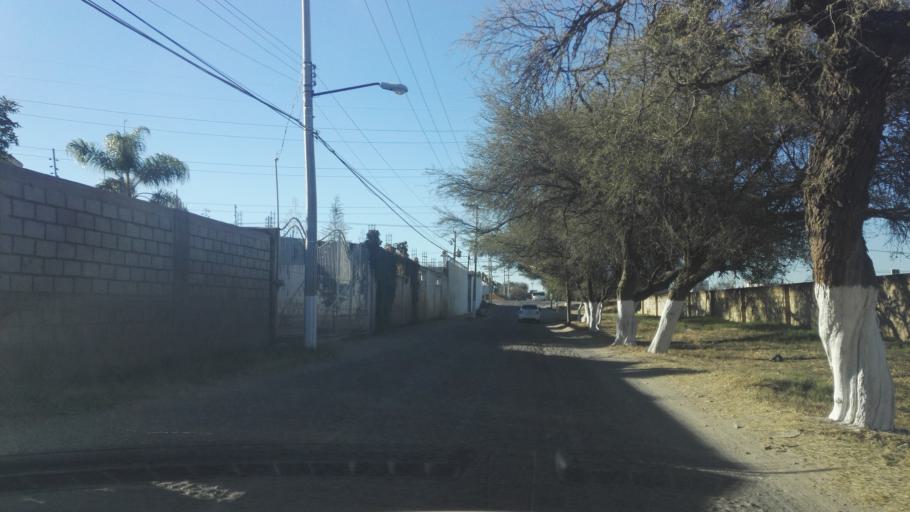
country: MX
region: Guanajuato
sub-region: Leon
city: Fraccionamiento Paraiso Real
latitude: 21.0715
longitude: -101.6006
